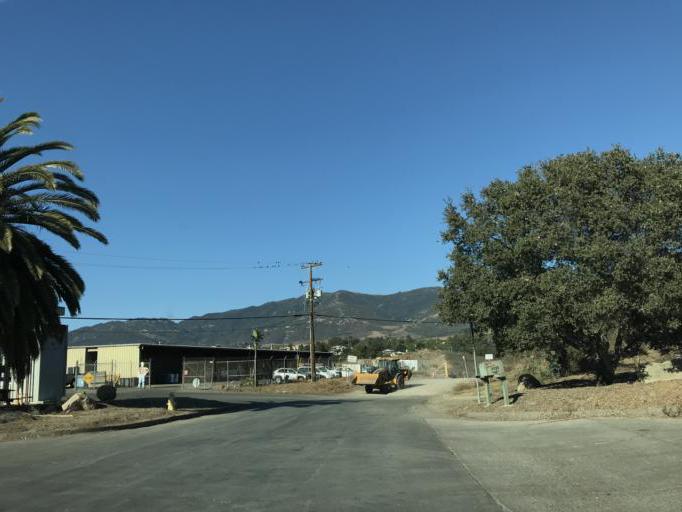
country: US
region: California
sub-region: Santa Barbara County
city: Goleta
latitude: 34.4491
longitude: -119.7735
